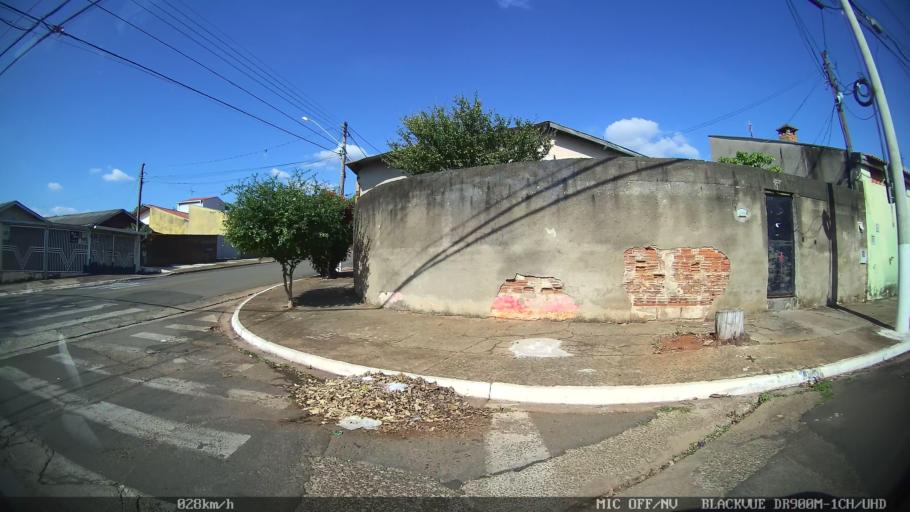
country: BR
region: Sao Paulo
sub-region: Sumare
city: Sumare
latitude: -22.8154
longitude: -47.2919
